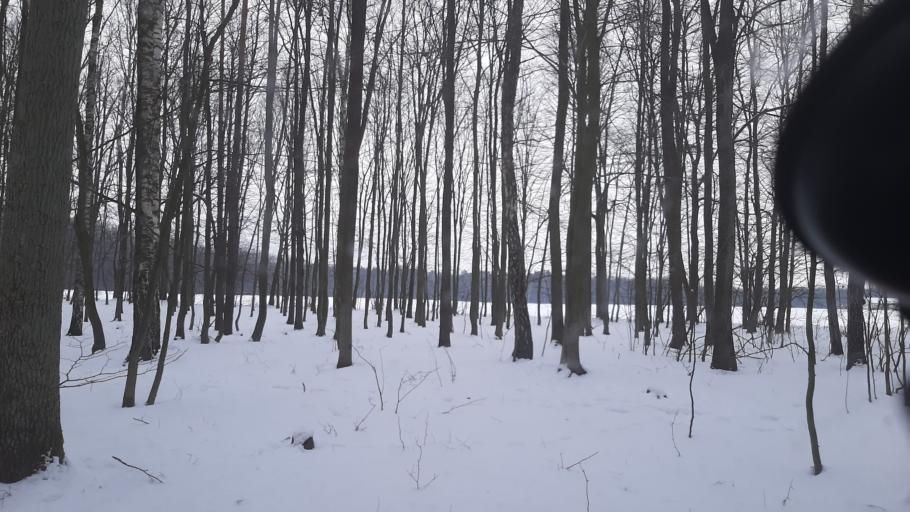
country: PL
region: Lublin Voivodeship
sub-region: Powiat lubelski
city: Garbow
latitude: 51.3732
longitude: 22.3928
